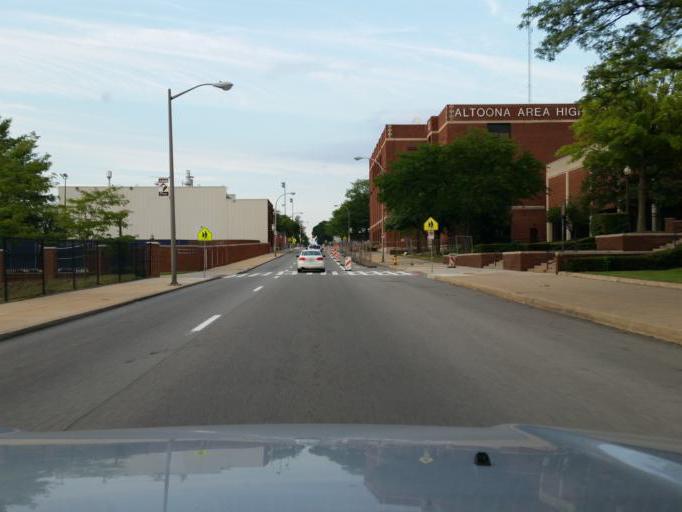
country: US
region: Pennsylvania
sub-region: Blair County
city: Altoona
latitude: 40.5090
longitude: -78.3992
